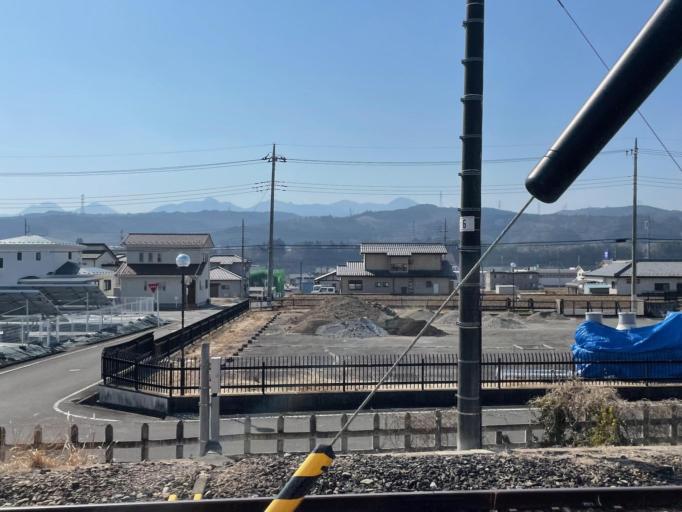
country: JP
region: Gunma
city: Nakanojomachi
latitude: 36.5854
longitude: 138.8526
